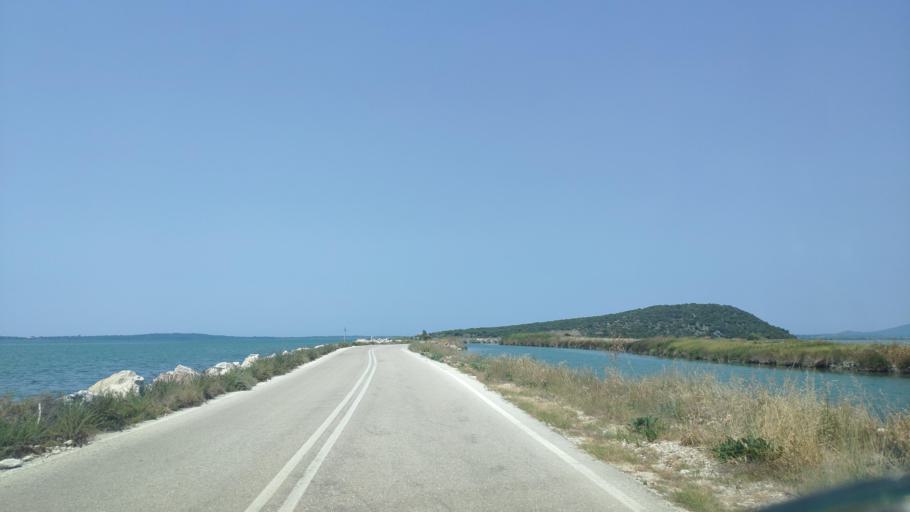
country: GR
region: Epirus
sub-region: Nomos Artas
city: Aneza
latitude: 39.0339
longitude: 20.8875
